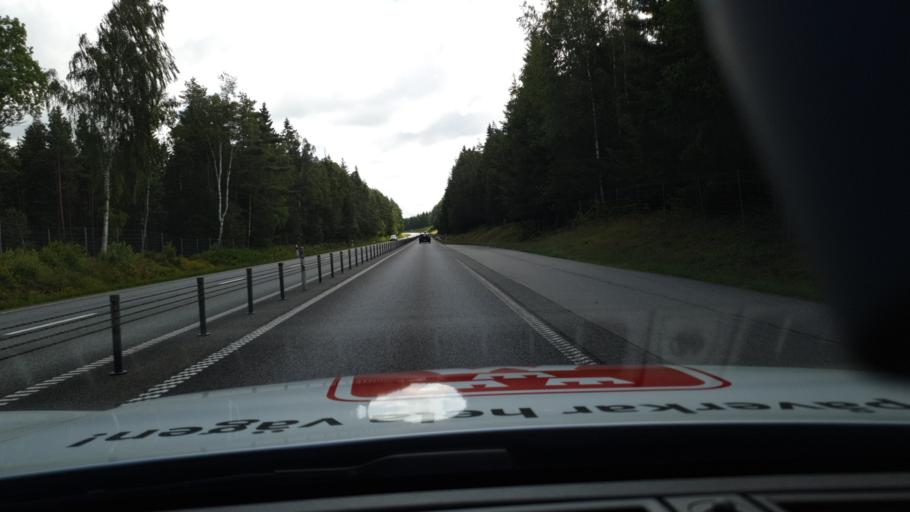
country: SE
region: Kronoberg
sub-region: Ljungby Kommun
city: Lagan
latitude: 56.8557
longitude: 14.0949
